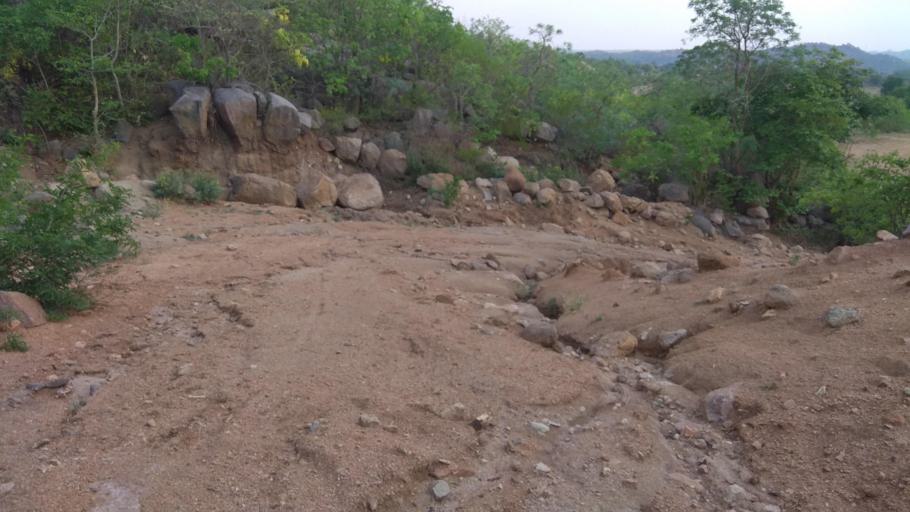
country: IN
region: Telangana
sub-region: Mahbubnagar
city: Farrukhnagar
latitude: 16.8904
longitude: 78.4964
